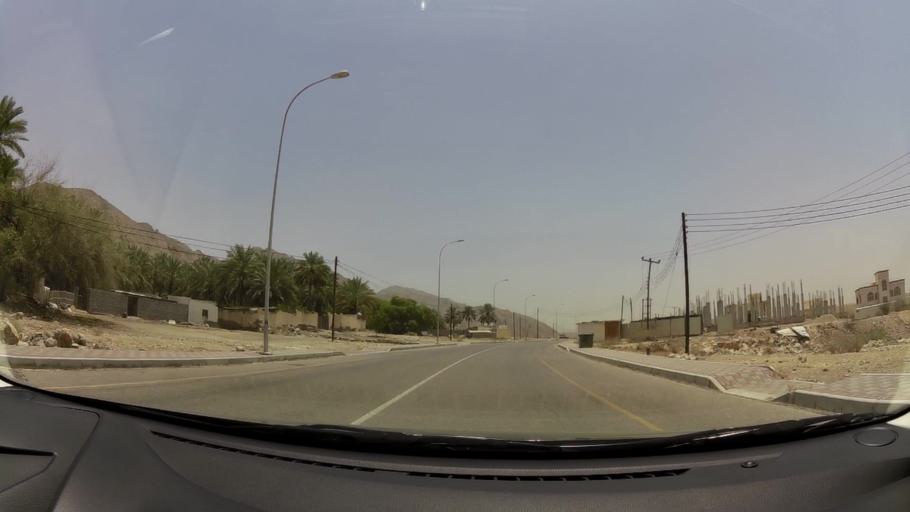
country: OM
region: Muhafazat Masqat
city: Bawshar
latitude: 23.5461
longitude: 58.4071
